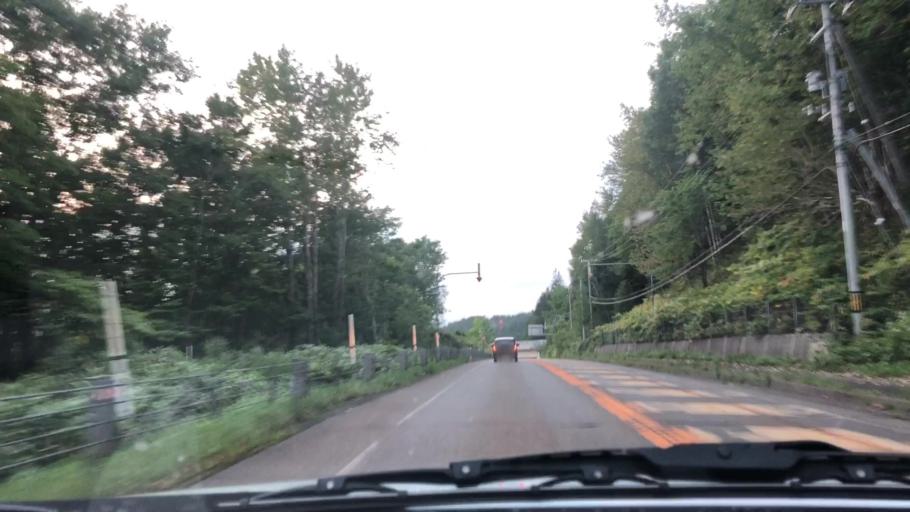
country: JP
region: Hokkaido
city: Iwamizawa
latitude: 42.9291
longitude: 142.0613
